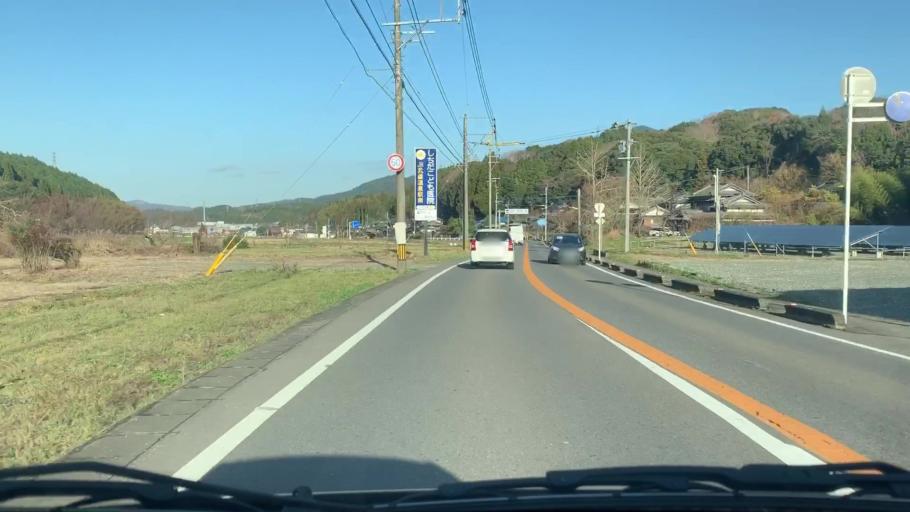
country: JP
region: Saga Prefecture
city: Takeocho-takeo
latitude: 33.2458
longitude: 130.0052
